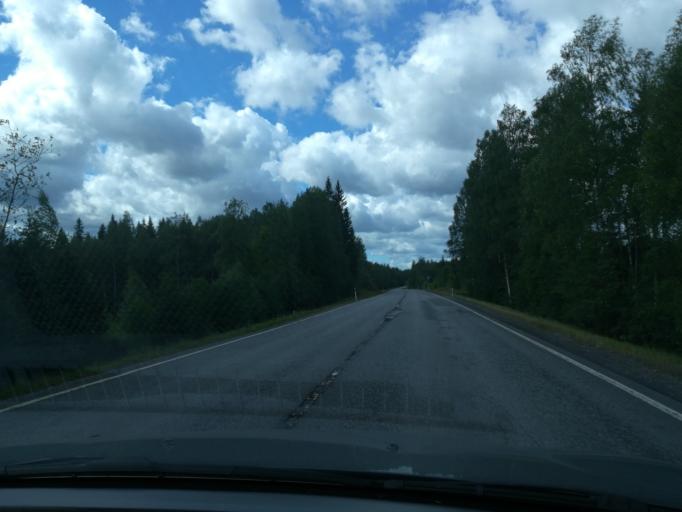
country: FI
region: Southern Savonia
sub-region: Mikkeli
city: Ristiina
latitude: 61.4263
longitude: 27.2253
